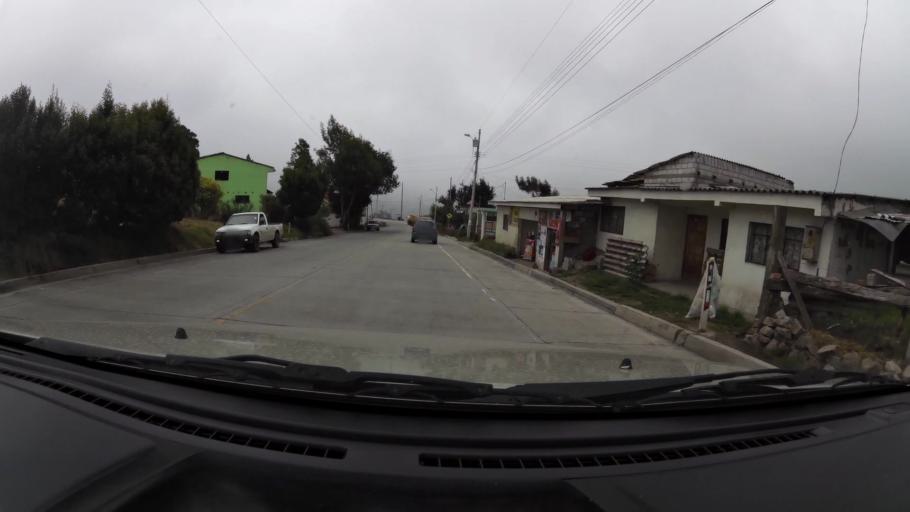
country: EC
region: Canar
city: Canar
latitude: -2.5648
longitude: -78.9271
